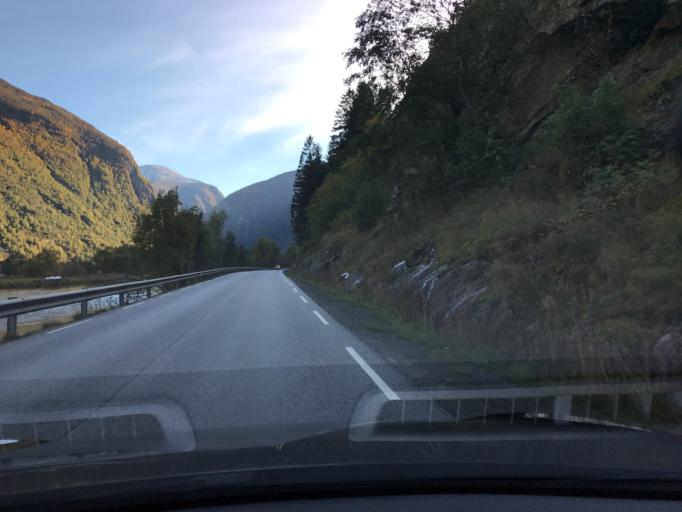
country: NO
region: Sogn og Fjordane
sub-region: Laerdal
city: Laerdalsoyri
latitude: 61.0951
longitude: 7.5178
